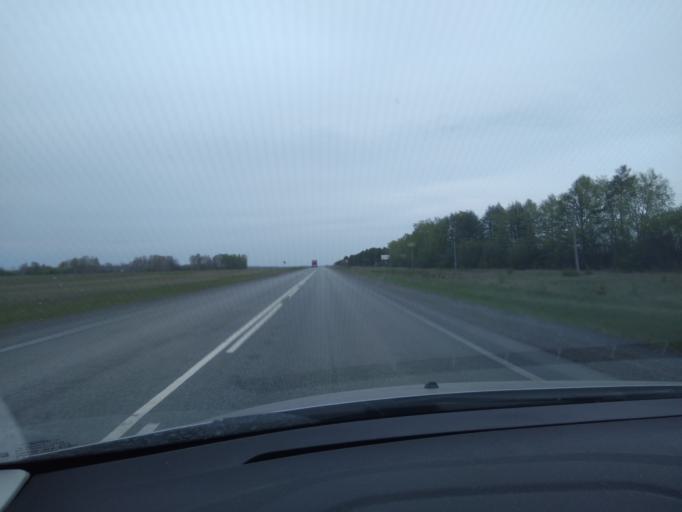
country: RU
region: Sverdlovsk
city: Talitsa
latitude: 57.0674
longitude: 63.5734
